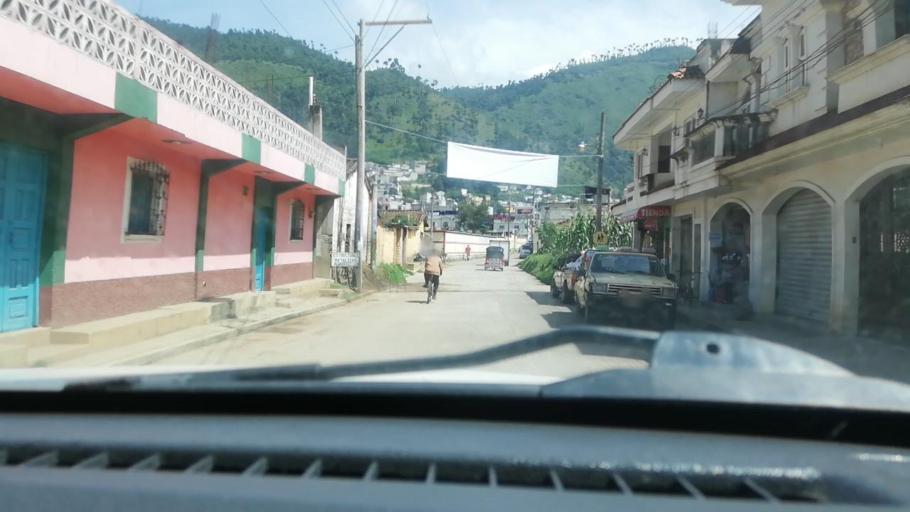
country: GT
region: Totonicapan
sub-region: Municipio de San Andres Xecul
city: San Andres Xecul
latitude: 14.9017
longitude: -91.4816
